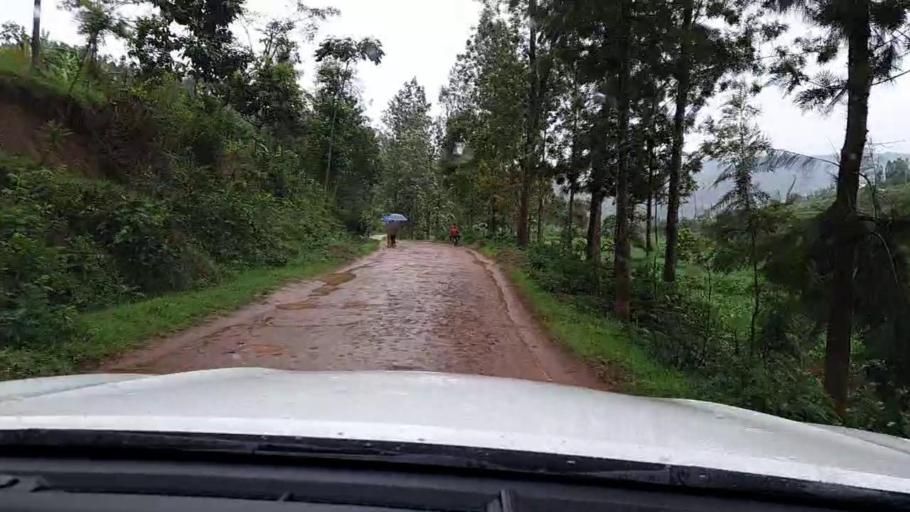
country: RW
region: Northern Province
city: Byumba
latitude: -1.7308
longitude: 29.9377
